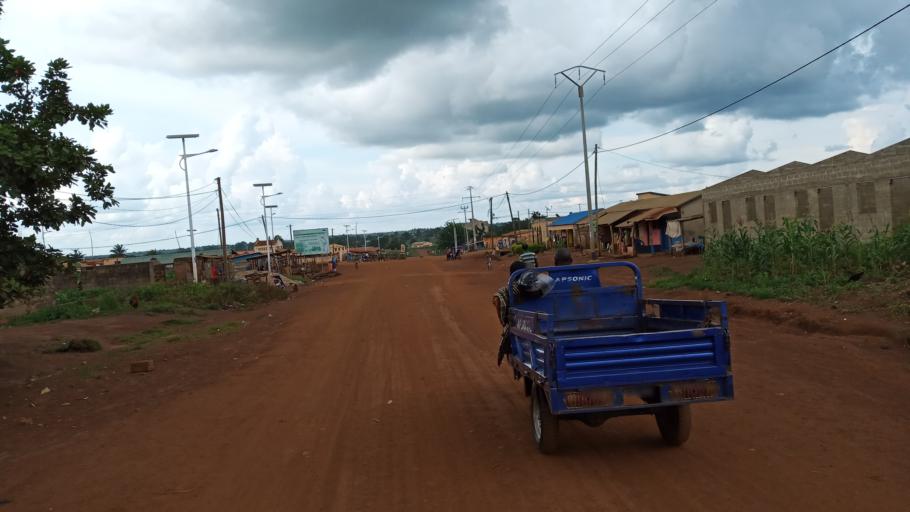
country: TG
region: Centrale
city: Sotouboua
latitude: 8.5572
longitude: 0.9848
